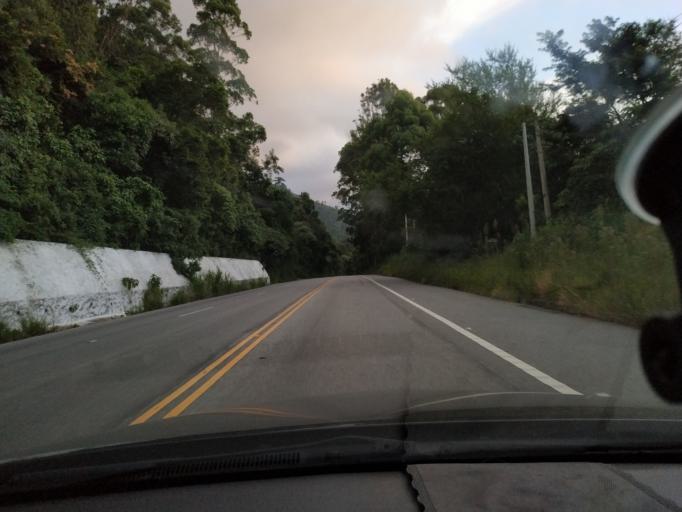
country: BR
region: Sao Paulo
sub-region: Campos Do Jordao
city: Campos do Jordao
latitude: -22.7993
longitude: -45.6259
